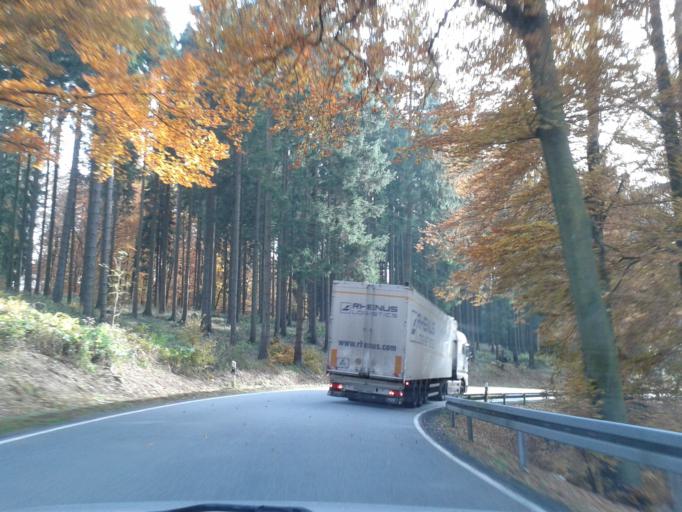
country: DE
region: North Rhine-Westphalia
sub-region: Regierungsbezirk Arnsberg
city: Bestwig
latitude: 51.3948
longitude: 8.4104
